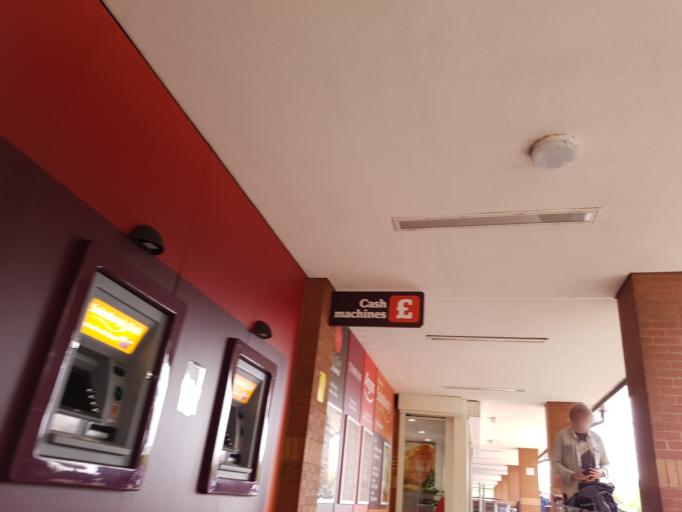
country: GB
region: England
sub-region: Nottingham
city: Nottingham
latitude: 52.9467
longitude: -1.1632
